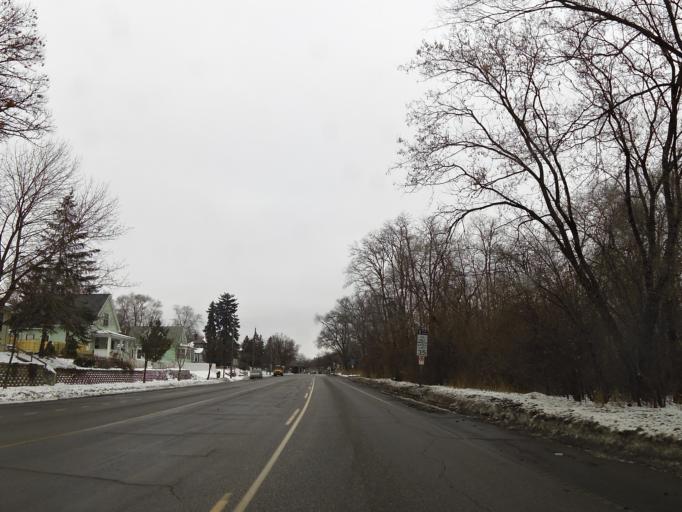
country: US
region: Minnesota
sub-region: Ramsey County
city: Saint Paul
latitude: 44.9250
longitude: -93.0651
